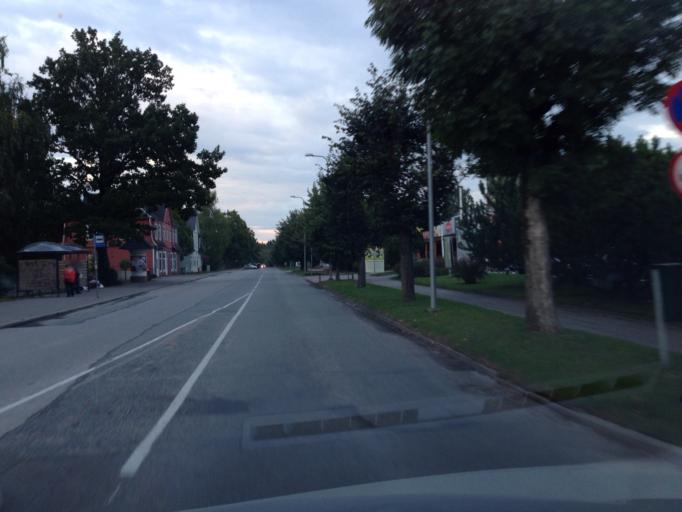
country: EE
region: Tartu
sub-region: Elva linn
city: Elva
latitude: 58.2214
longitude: 26.4069
